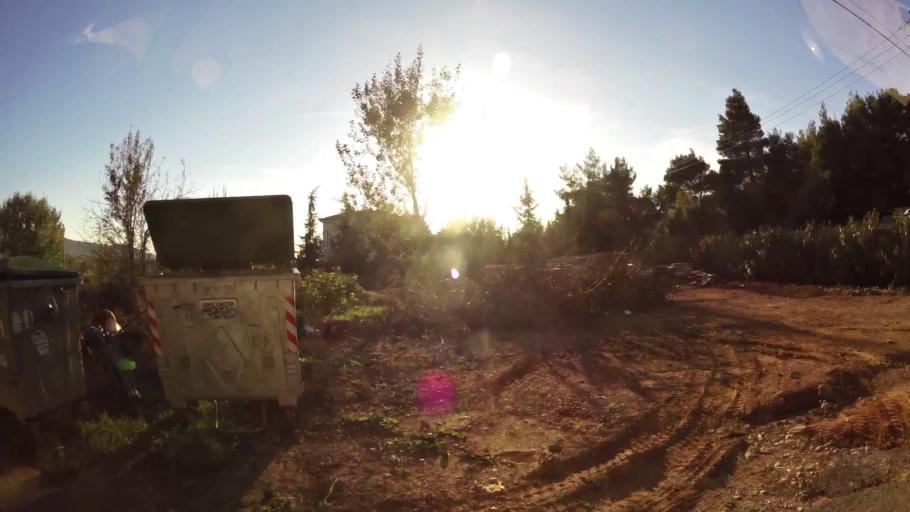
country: GR
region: Attica
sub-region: Nomarchia Anatolikis Attikis
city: Anoixi
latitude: 38.1357
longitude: 23.8507
